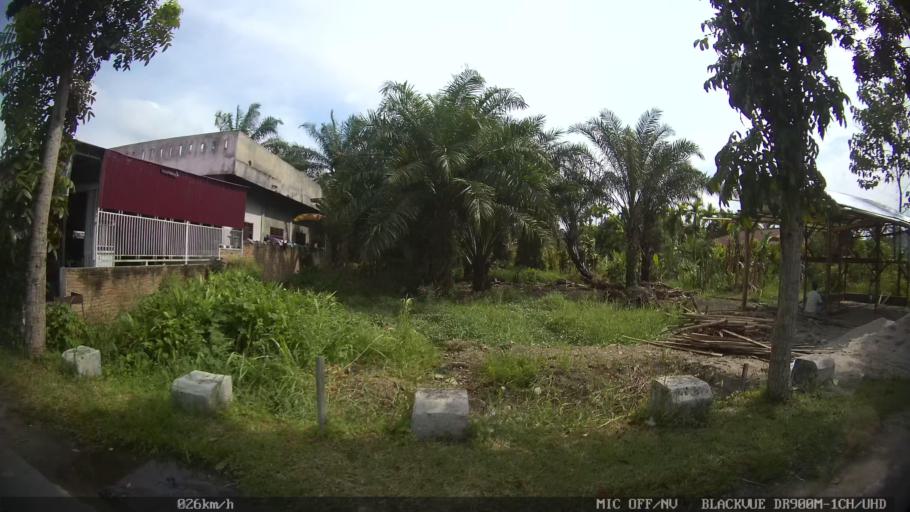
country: ID
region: North Sumatra
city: Percut
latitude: 3.6111
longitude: 98.8297
